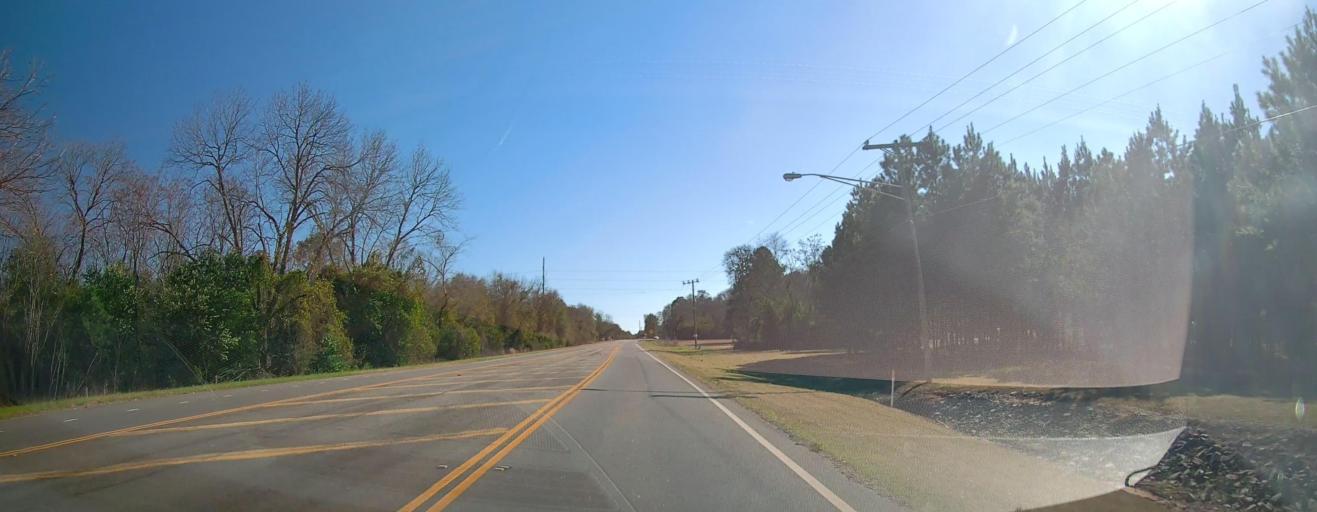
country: US
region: Georgia
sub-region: Macon County
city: Oglethorpe
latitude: 32.2563
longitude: -84.0858
